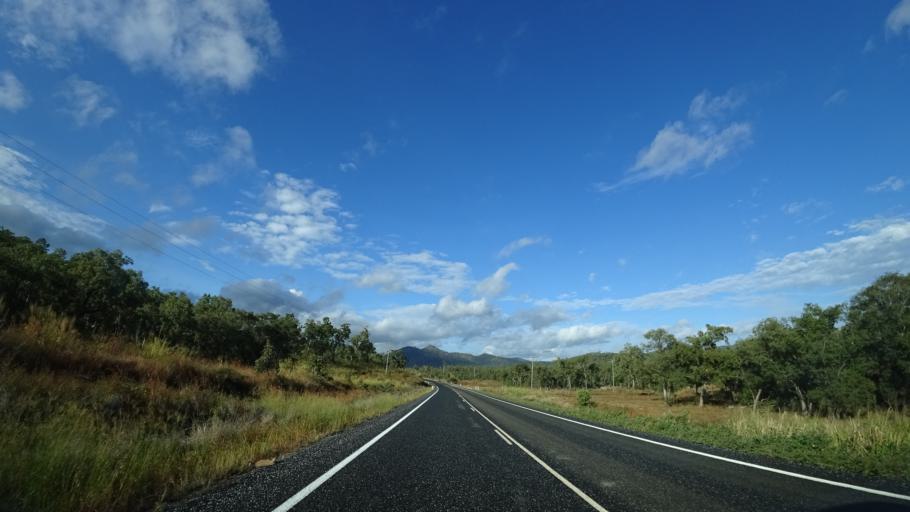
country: AU
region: Queensland
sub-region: Cook
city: Cooktown
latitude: -15.6063
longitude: 145.2221
